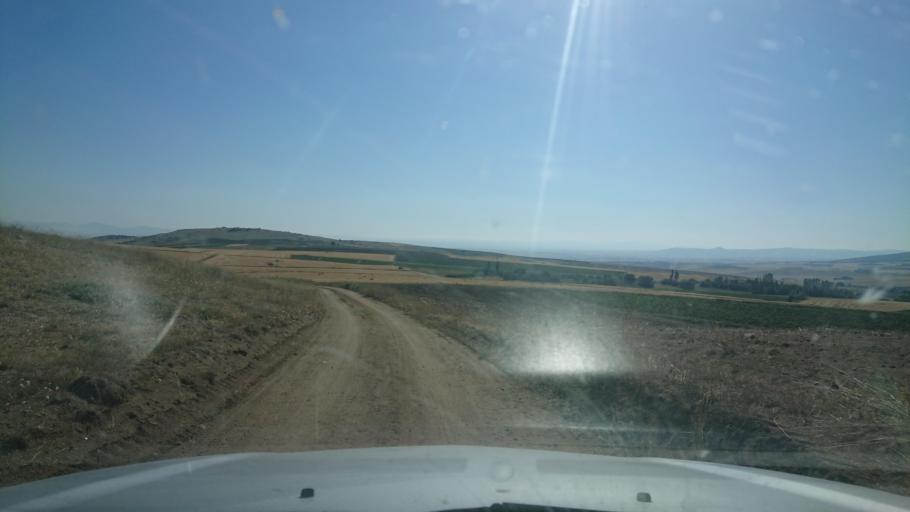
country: TR
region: Aksaray
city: Agacoren
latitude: 38.8343
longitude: 33.9457
